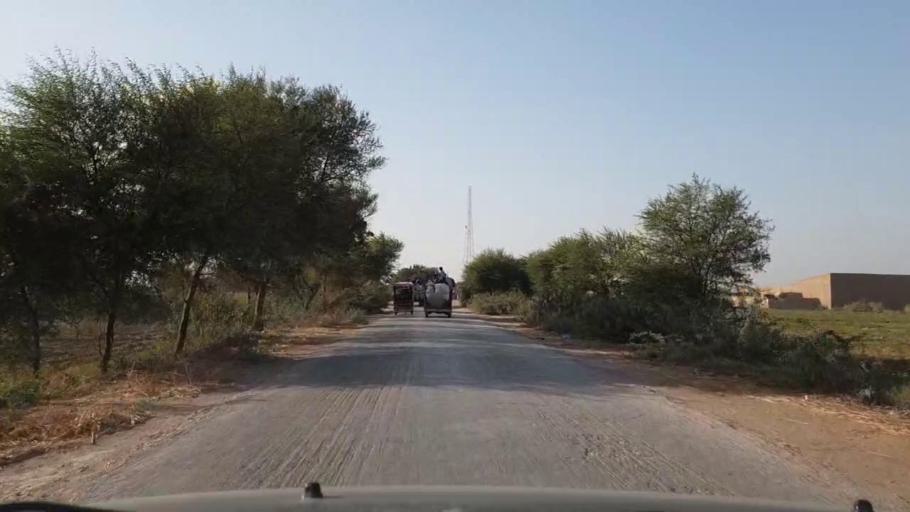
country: PK
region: Sindh
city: Chambar
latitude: 25.2107
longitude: 68.7811
